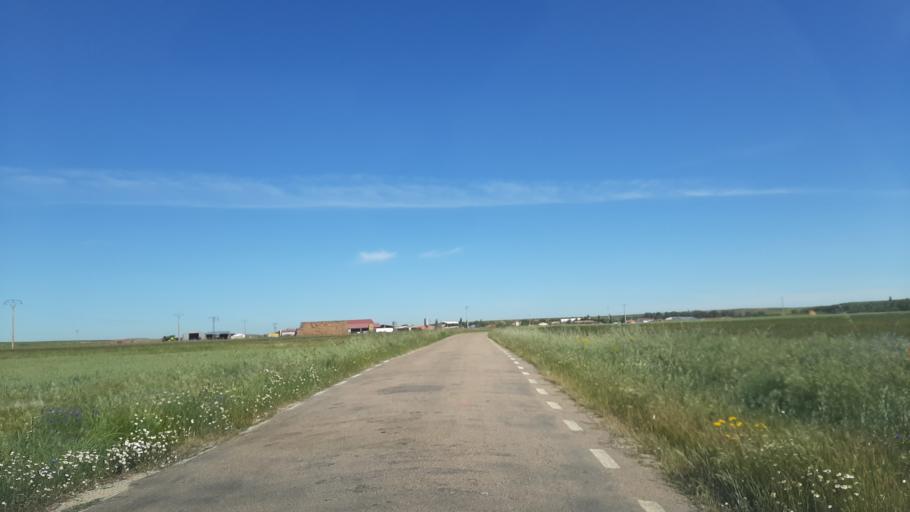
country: ES
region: Castille and Leon
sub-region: Provincia de Salamanca
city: Pedrosillo de Alba
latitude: 40.8153
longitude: -5.3884
